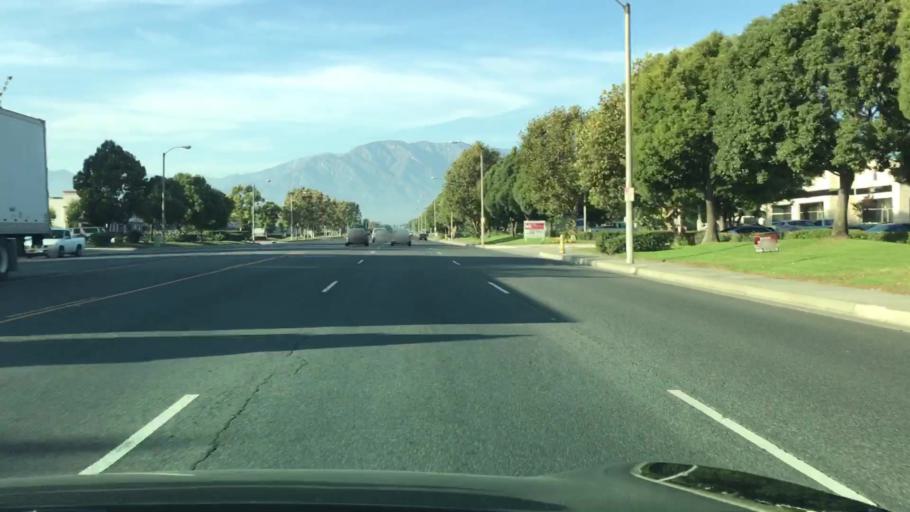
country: US
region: California
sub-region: San Bernardino County
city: Ontario
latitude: 34.0353
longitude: -117.6284
